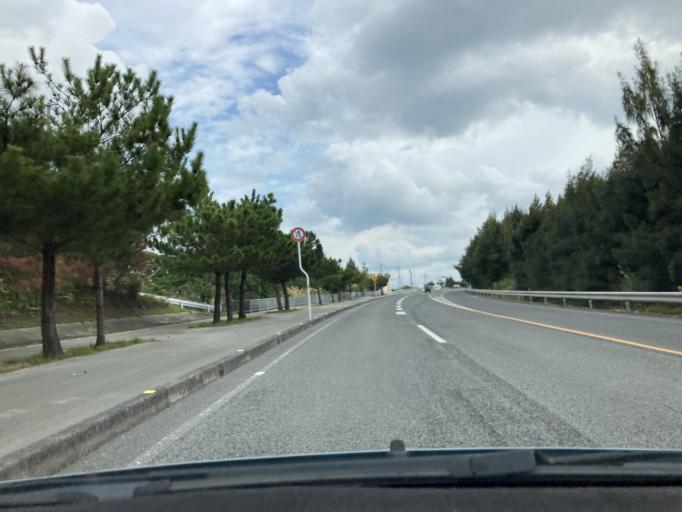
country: JP
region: Okinawa
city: Ishikawa
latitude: 26.4461
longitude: 127.8082
